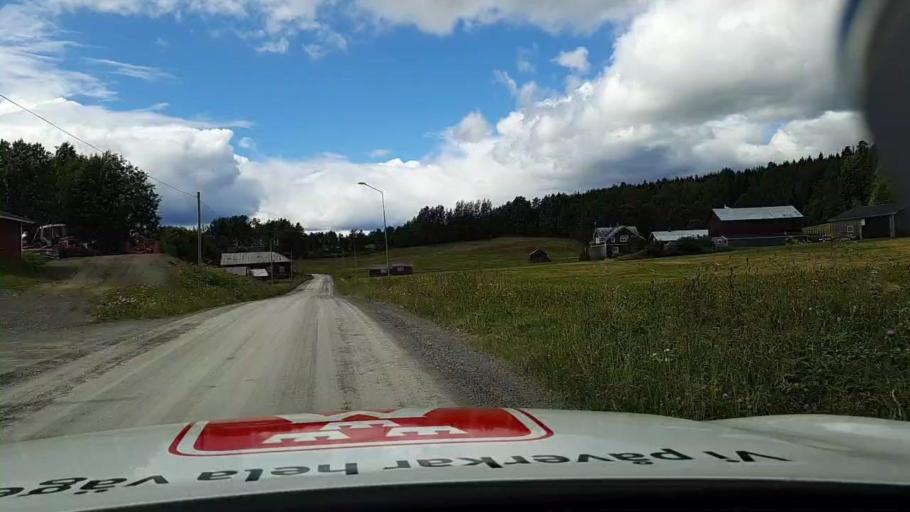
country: SE
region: Jaemtland
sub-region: Krokoms Kommun
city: Krokom
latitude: 63.5684
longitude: 14.2579
